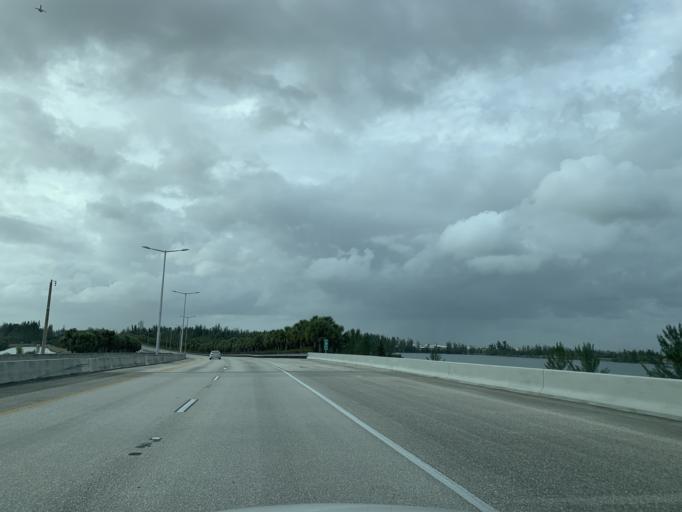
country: US
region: Florida
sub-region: Miami-Dade County
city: Tamiami
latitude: 25.7835
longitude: -80.3930
